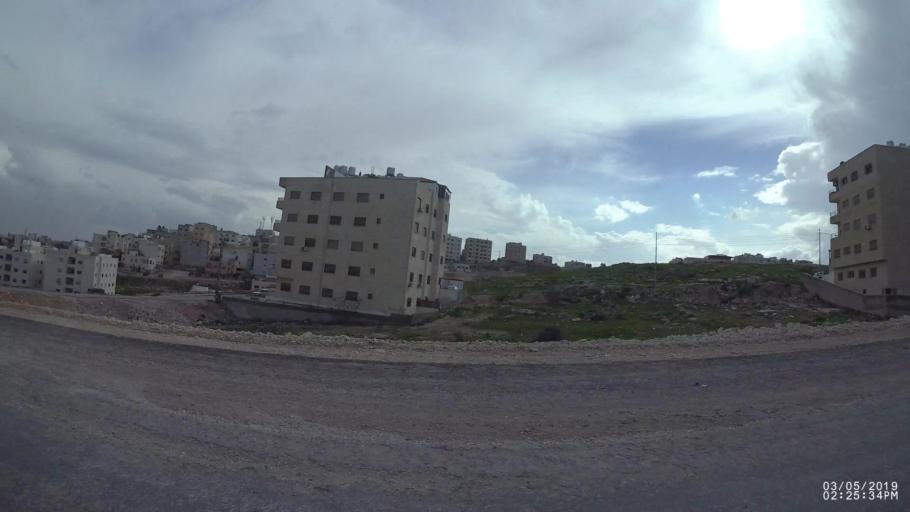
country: JO
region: Amman
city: Amman
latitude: 32.0163
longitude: 35.9430
